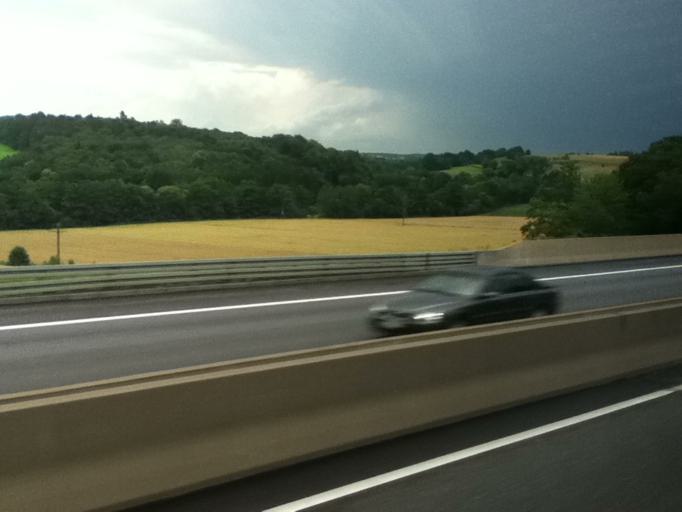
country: DE
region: Hesse
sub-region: Regierungsbezirk Giessen
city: Homberg
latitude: 50.6715
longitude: 9.0248
